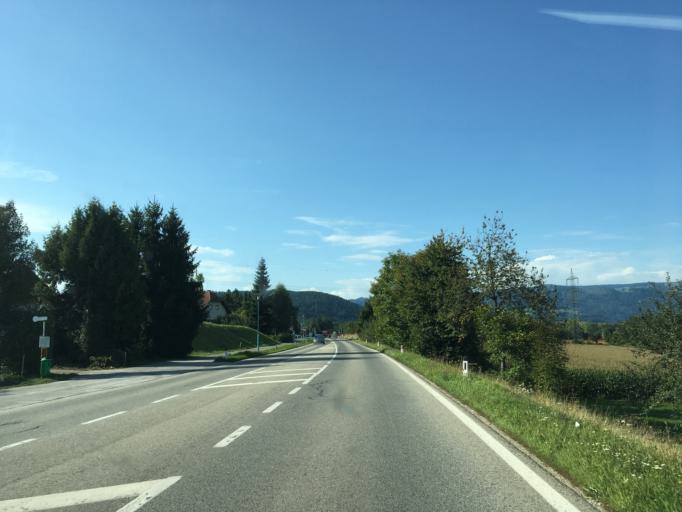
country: AT
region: Carinthia
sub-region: Politischer Bezirk Volkermarkt
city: Voelkermarkt
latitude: 46.6305
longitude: 14.6338
